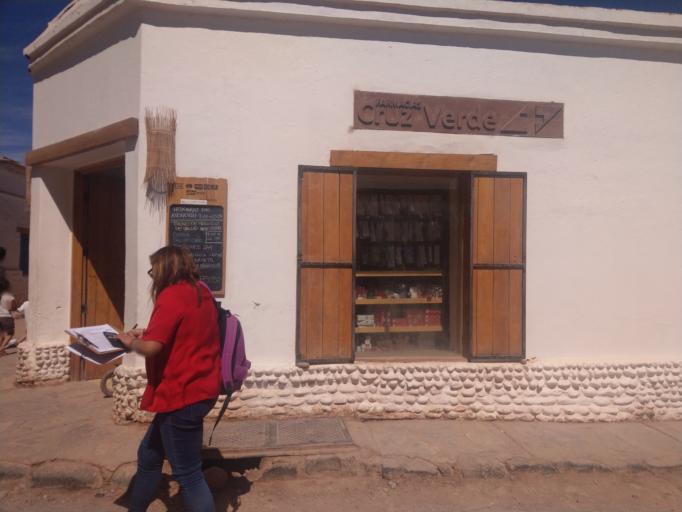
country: CL
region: Antofagasta
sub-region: Provincia de El Loa
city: San Pedro de Atacama
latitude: -22.9116
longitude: -68.1999
